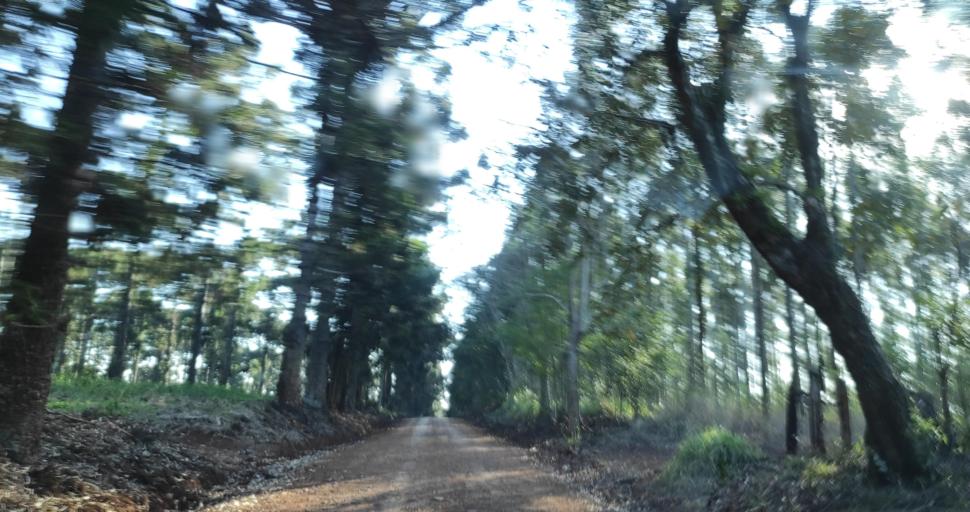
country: AR
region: Misiones
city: Capiovi
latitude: -26.8736
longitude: -55.1128
